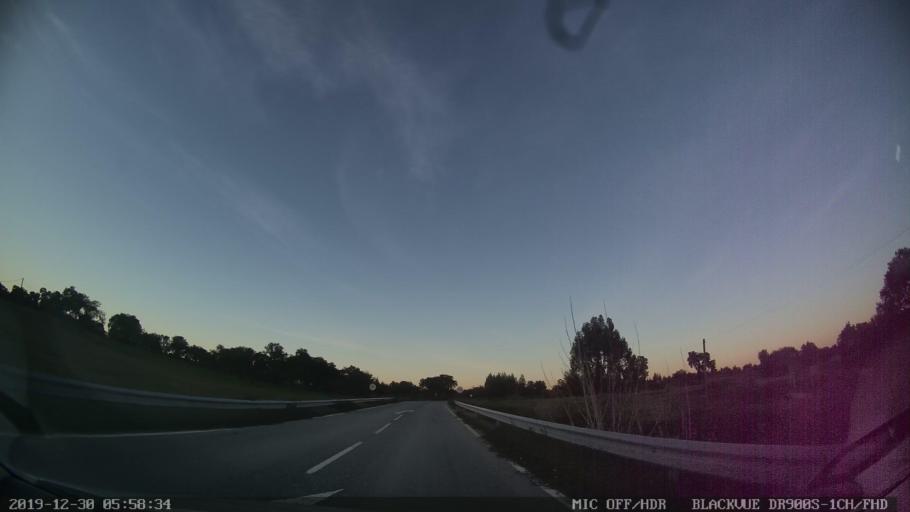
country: PT
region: Castelo Branco
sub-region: Idanha-A-Nova
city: Idanha-a-Nova
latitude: 40.0359
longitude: -7.2425
